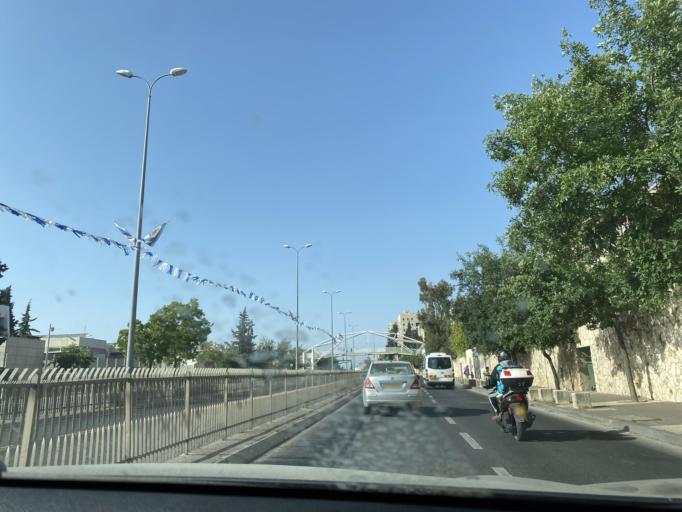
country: IL
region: Jerusalem
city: Jerusalem
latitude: 31.7479
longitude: 35.2180
